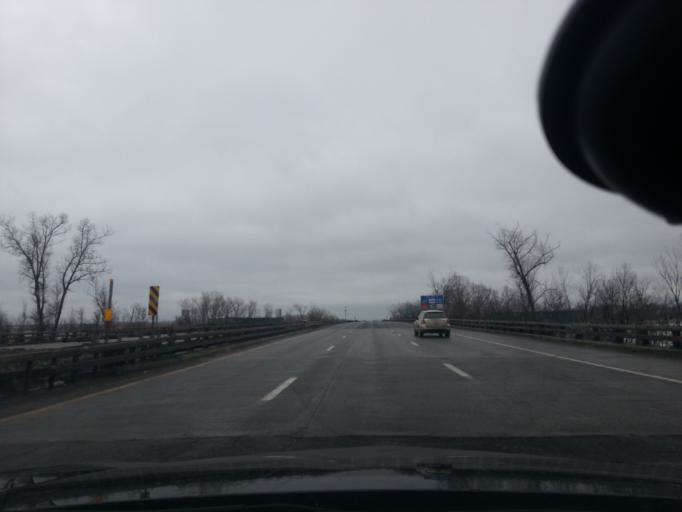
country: US
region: New York
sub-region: Onondaga County
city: Brewerton
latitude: 43.2420
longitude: -76.1313
